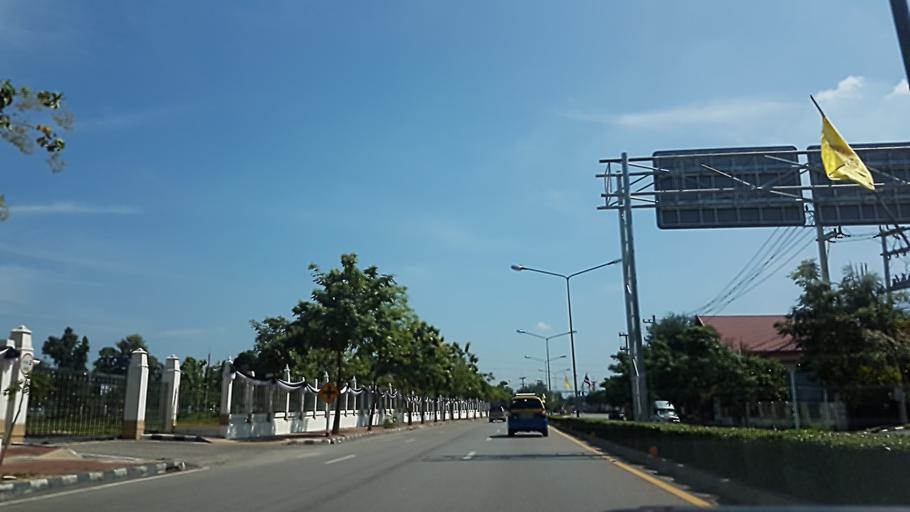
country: TH
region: Chiang Mai
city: Chiang Mai
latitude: 18.8238
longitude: 98.9634
